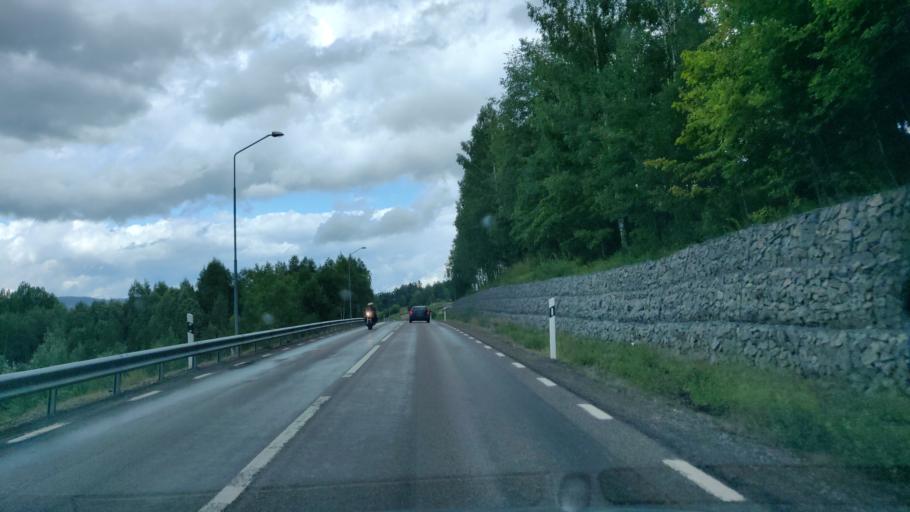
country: SE
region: Vaermland
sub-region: Torsby Kommun
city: Torsby
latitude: 60.6016
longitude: 13.0634
